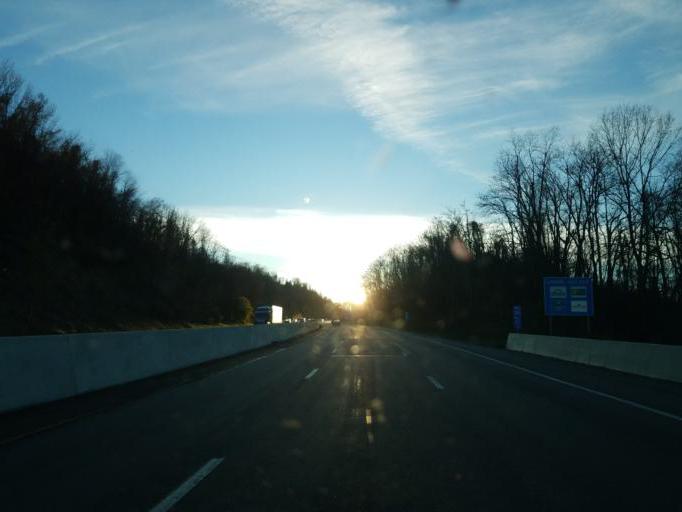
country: US
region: Ohio
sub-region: Belmont County
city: Wolfhurst
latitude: 40.0650
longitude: -80.8206
